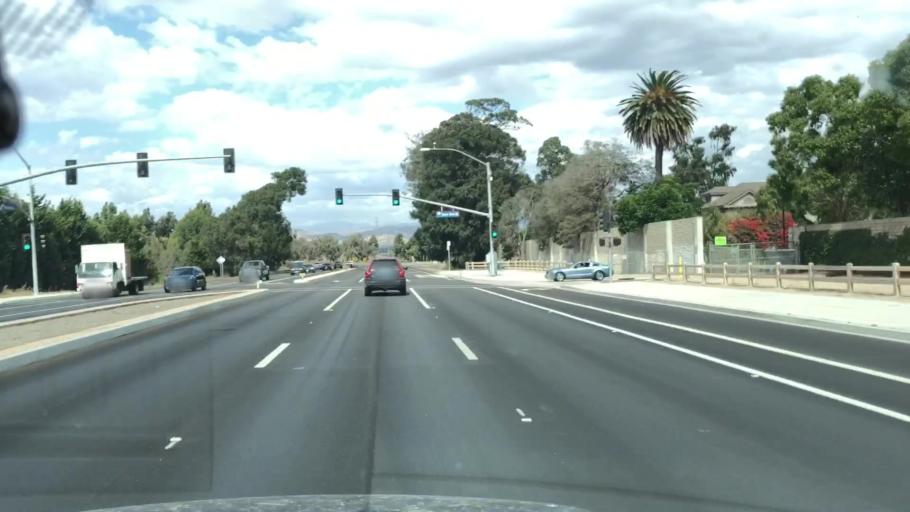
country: US
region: California
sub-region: Ventura County
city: Oxnard Shores
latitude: 34.2246
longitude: -119.2210
